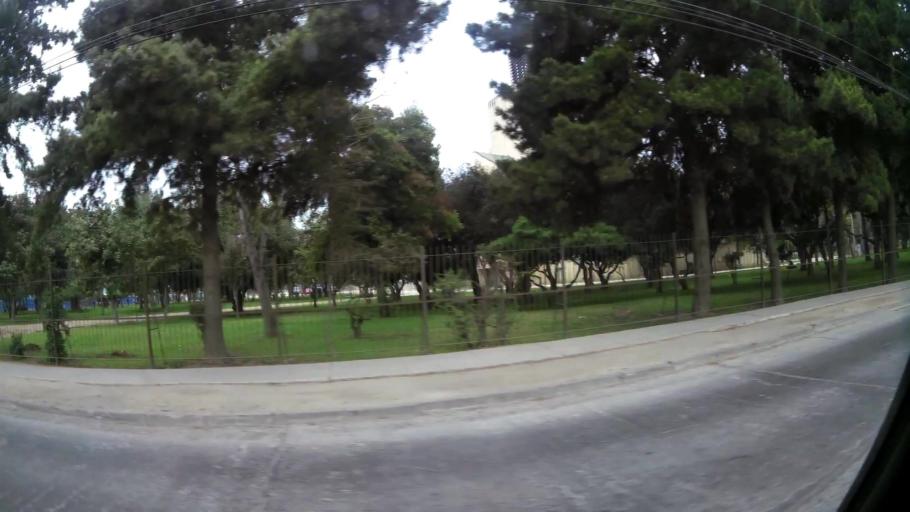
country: CL
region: Santiago Metropolitan
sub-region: Provincia de Santiago
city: Lo Prado
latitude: -33.5104
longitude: -70.7671
